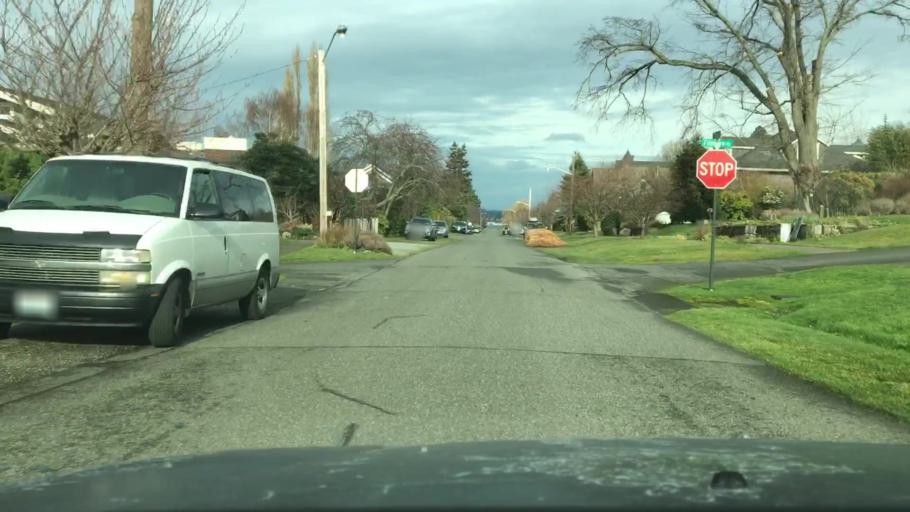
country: US
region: Washington
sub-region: Whatcom County
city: Bellingham
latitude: 48.7246
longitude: -122.5015
